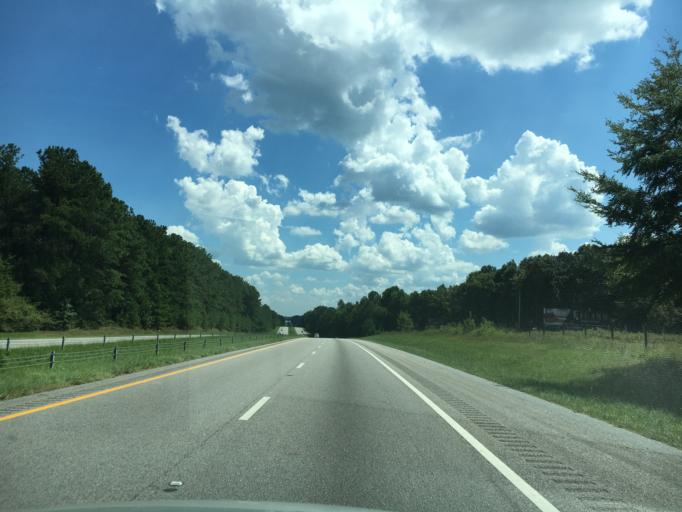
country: US
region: South Carolina
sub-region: Laurens County
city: Clinton
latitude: 34.5611
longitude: -81.8910
